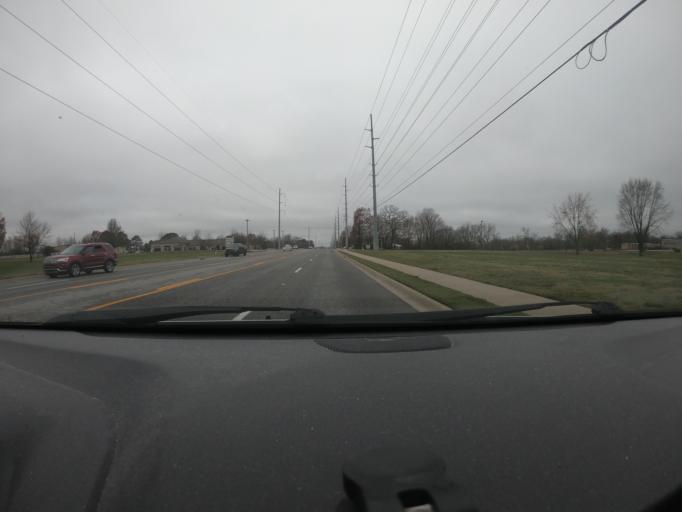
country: US
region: Arkansas
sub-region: Benton County
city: Bentonville
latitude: 36.3574
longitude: -94.2284
